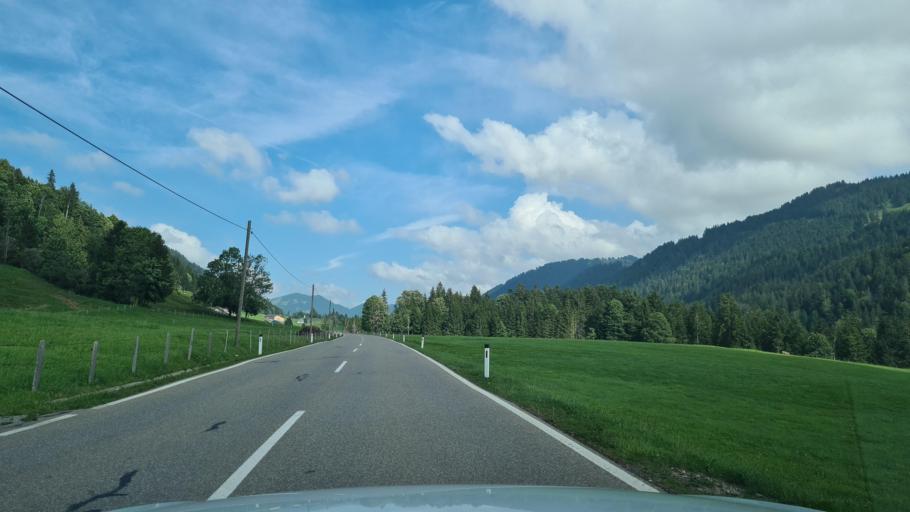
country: AT
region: Vorarlberg
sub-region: Politischer Bezirk Bregenz
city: Sibratsgfall
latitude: 47.4482
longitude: 10.0196
